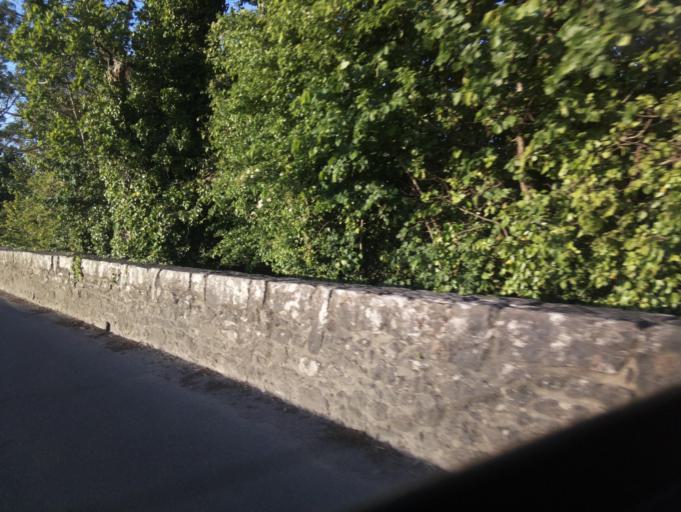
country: GB
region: England
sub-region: Devon
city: Newton Abbot
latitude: 50.5472
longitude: -3.6166
